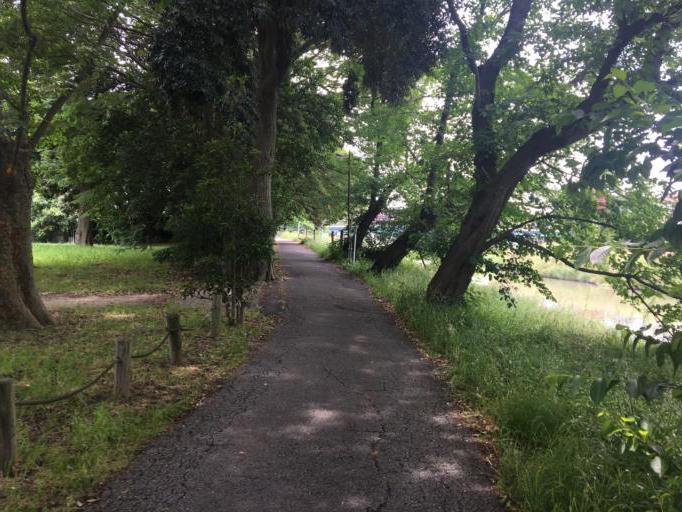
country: JP
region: Saitama
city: Koshigaya
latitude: 35.8971
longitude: 139.7861
